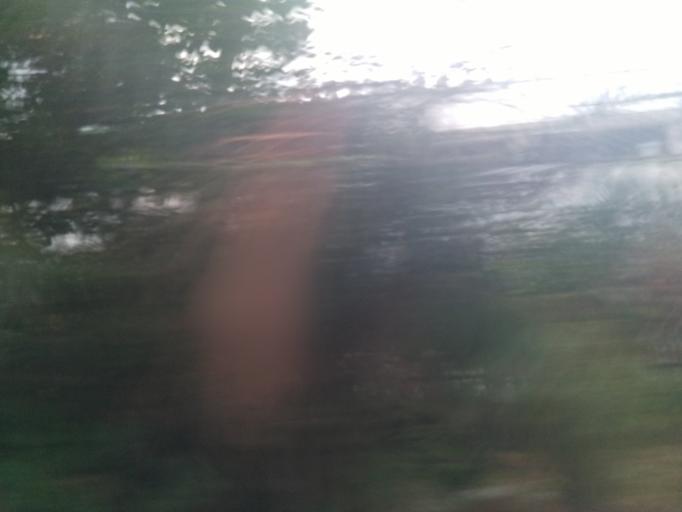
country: TZ
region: Dar es Salaam
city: Dar es Salaam
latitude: -6.8016
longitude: 39.2877
